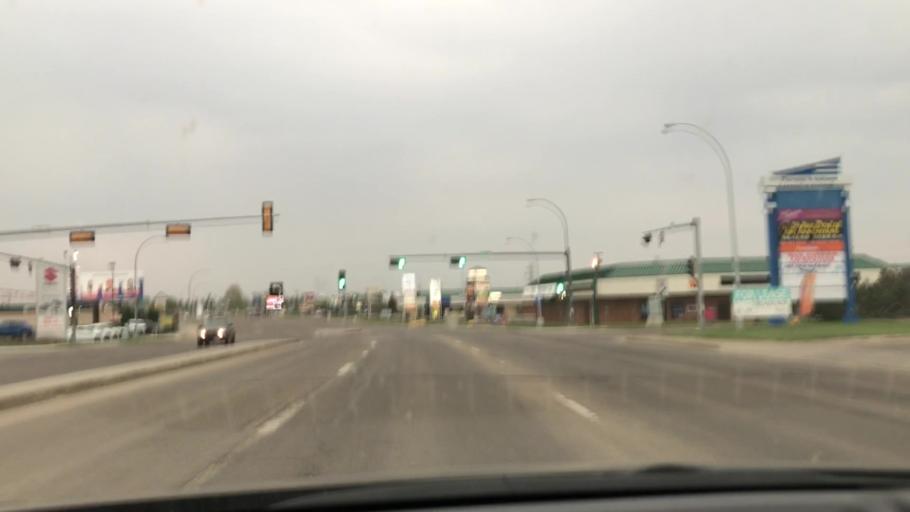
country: CA
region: Alberta
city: Edmonton
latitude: 53.4661
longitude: -113.4759
